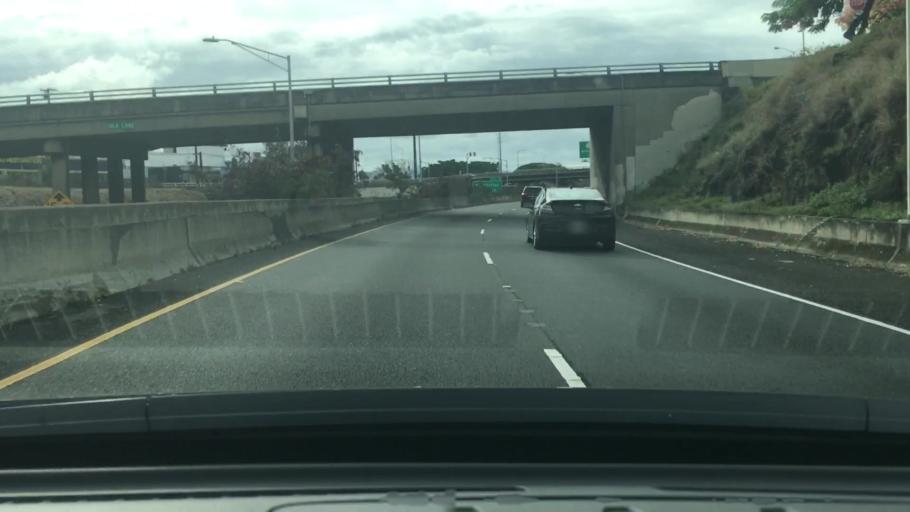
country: US
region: Hawaii
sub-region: Honolulu County
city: Honolulu
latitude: 21.3367
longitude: -157.8820
